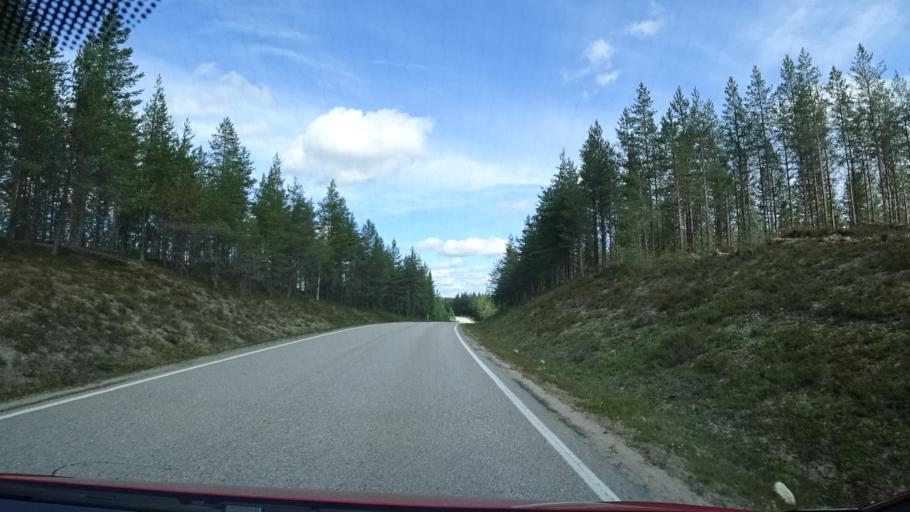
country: FI
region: Kainuu
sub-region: Kehys-Kainuu
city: Kuhmo
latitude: 64.6470
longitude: 29.6778
